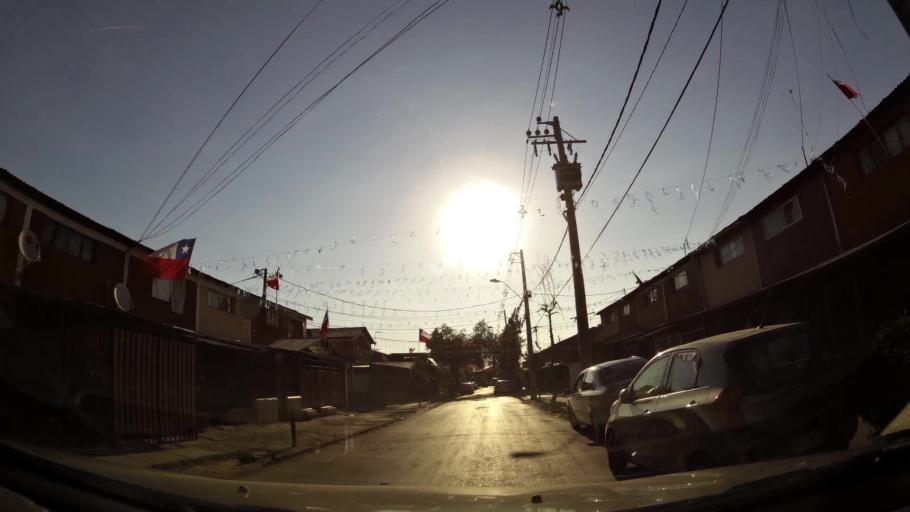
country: CL
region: Santiago Metropolitan
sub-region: Provincia de Santiago
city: La Pintana
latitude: -33.5799
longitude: -70.6628
